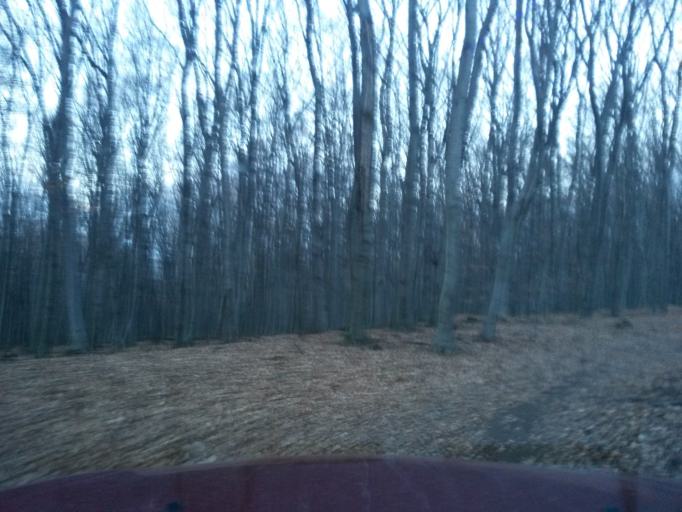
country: SK
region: Kosicky
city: Kosice
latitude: 48.7045
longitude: 21.3691
